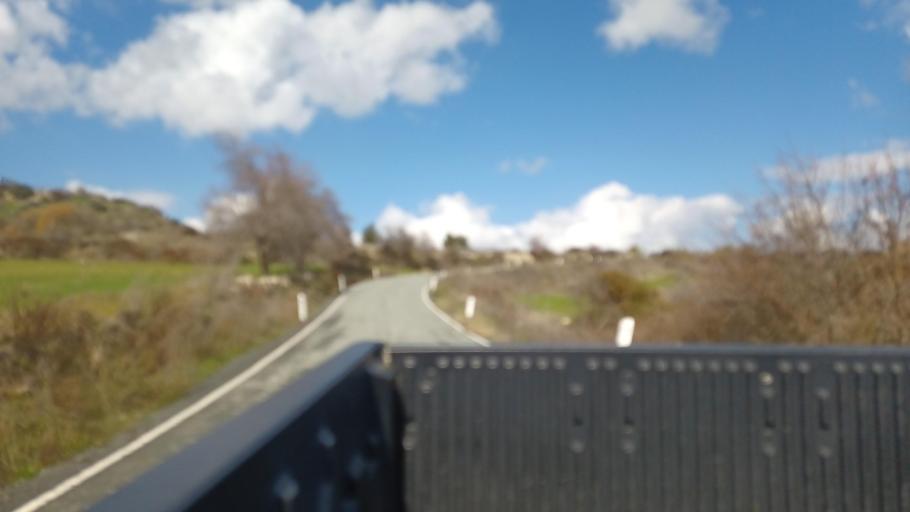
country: CY
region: Limassol
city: Pachna
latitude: 34.7772
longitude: 32.7462
